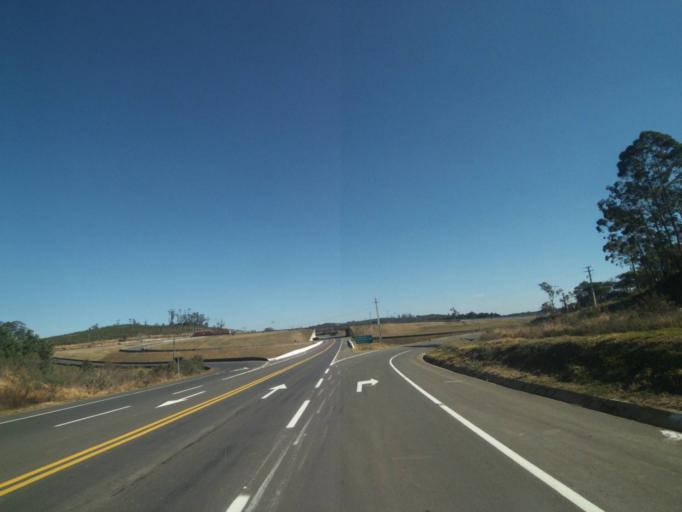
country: BR
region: Parana
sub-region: Tibagi
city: Tibagi
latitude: -24.8137
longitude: -50.4850
